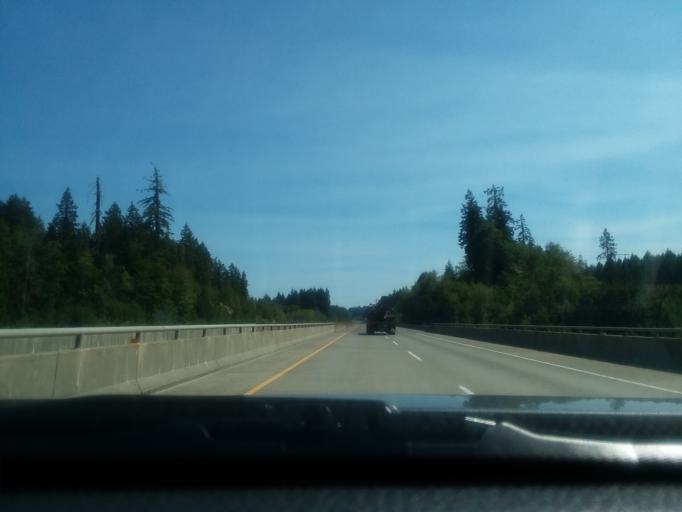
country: CA
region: British Columbia
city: Port Alberni
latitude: 49.4411
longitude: -124.7586
